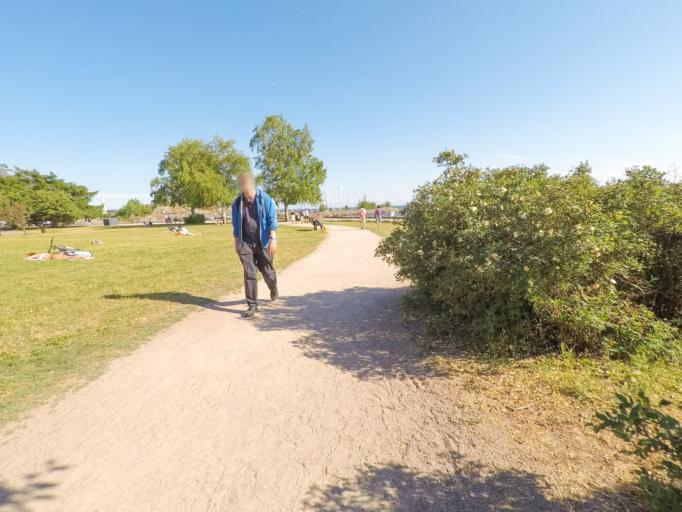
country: FI
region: Uusimaa
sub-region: Helsinki
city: Helsinki
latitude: 60.1540
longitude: 24.9381
